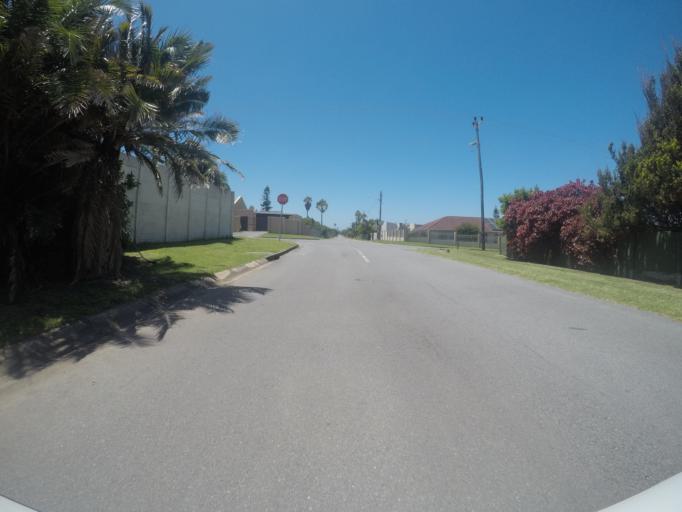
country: ZA
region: Eastern Cape
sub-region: Buffalo City Metropolitan Municipality
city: East London
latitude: -32.9494
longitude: 28.0138
